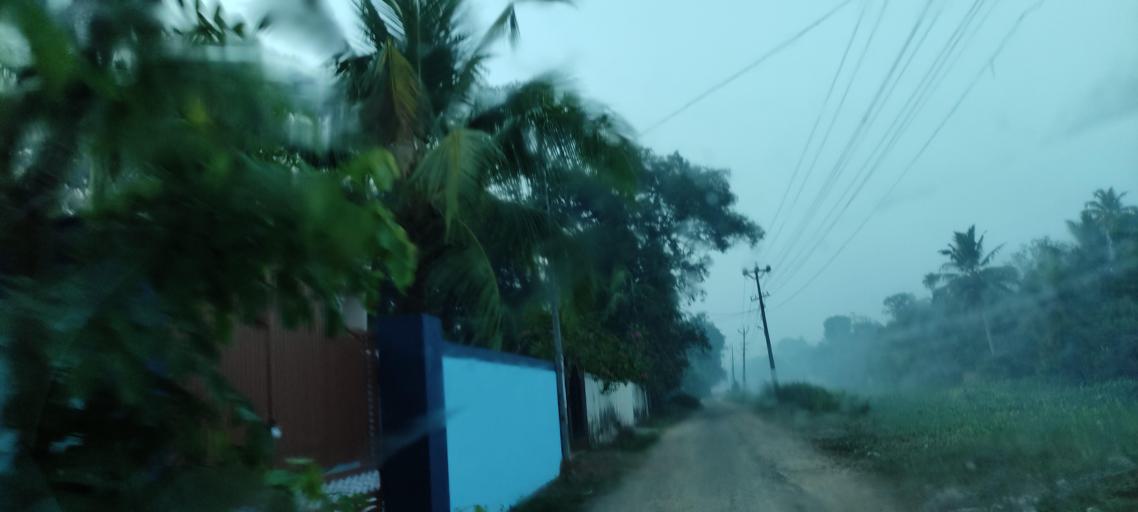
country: IN
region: Kerala
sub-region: Alappuzha
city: Alleppey
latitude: 9.5313
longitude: 76.3294
